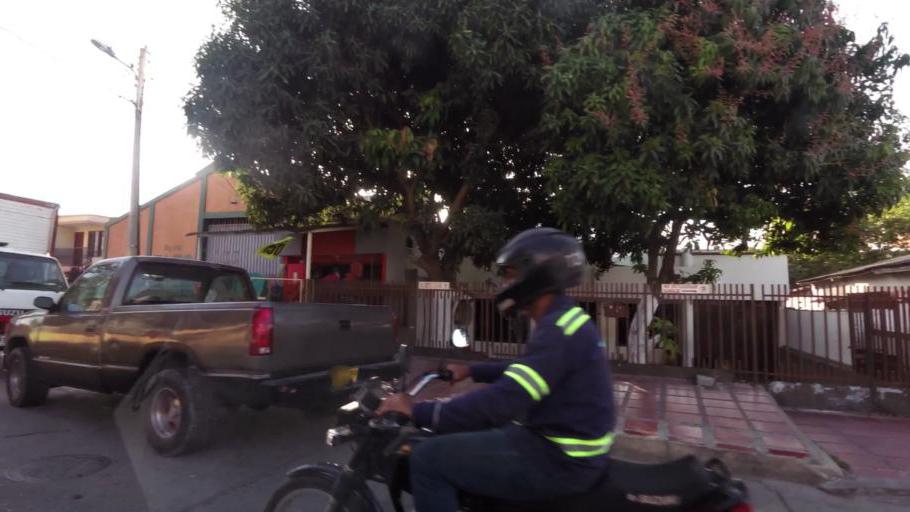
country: CO
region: Bolivar
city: Cartagena
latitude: 10.3930
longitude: -75.5195
